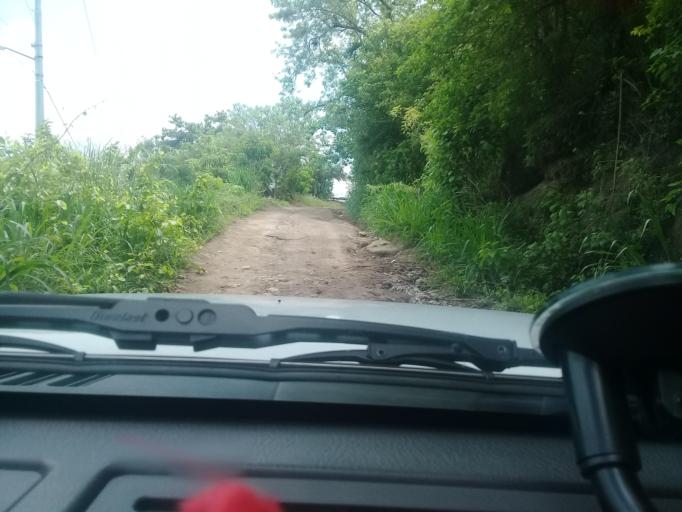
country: MX
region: Veracruz
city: Paso de Ovejas
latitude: 19.2837
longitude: -96.4301
